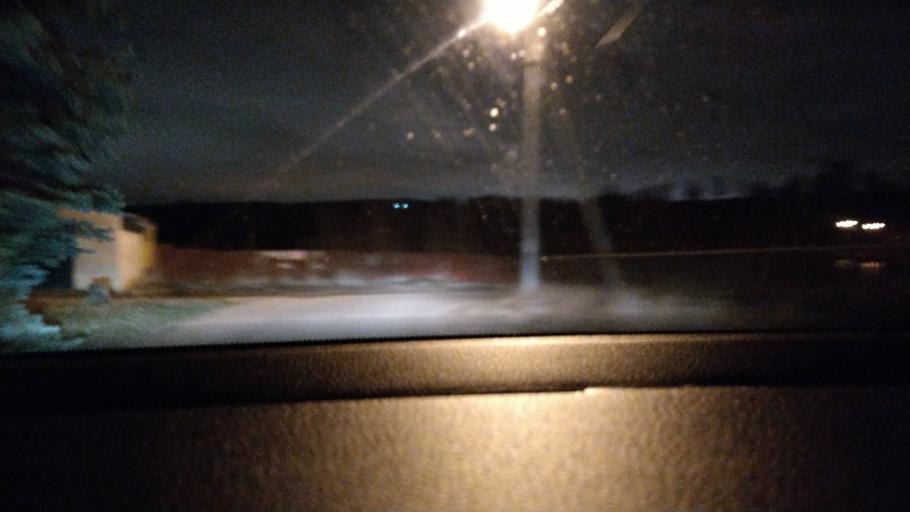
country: RU
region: Moskovskaya
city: Novopodrezkovo
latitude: 55.9224
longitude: 37.3468
